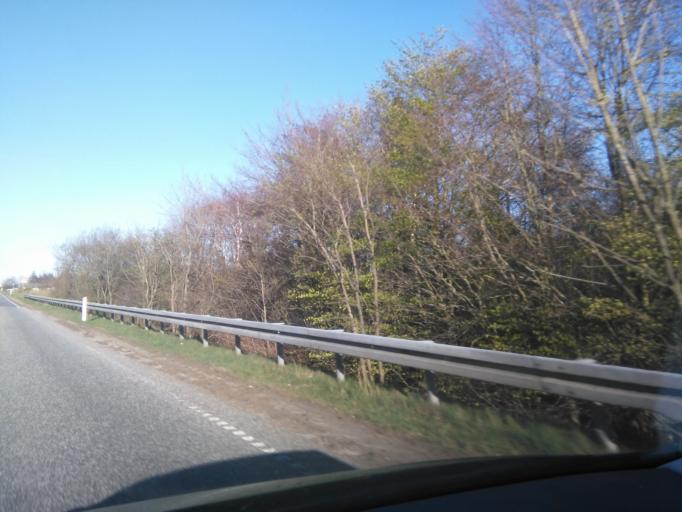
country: DK
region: Central Jutland
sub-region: Herning Kommune
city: Vildbjerg
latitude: 56.1114
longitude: 8.7559
